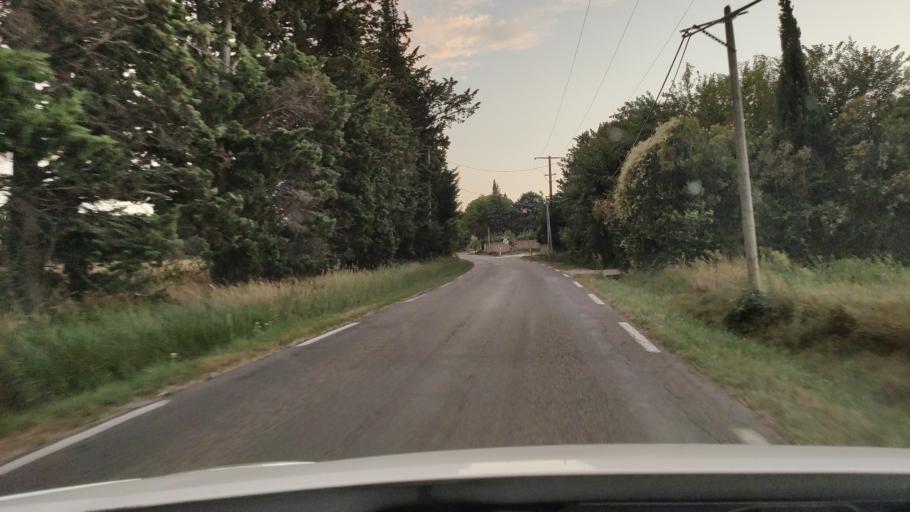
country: FR
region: Provence-Alpes-Cote d'Azur
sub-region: Departement du Vaucluse
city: Velleron
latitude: 43.9508
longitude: 5.0193
